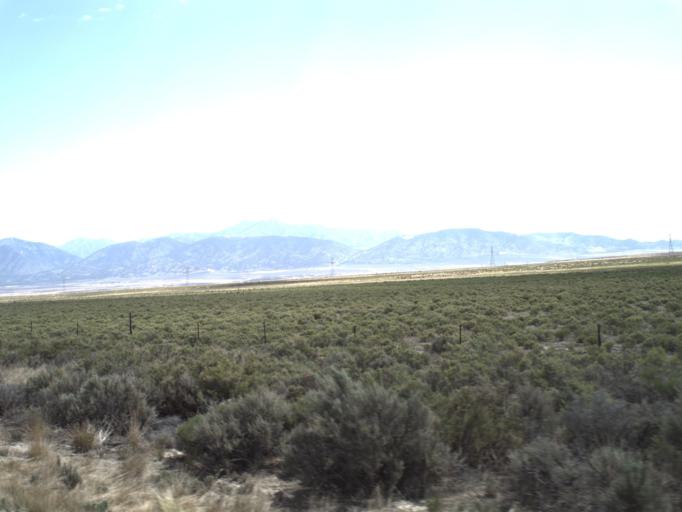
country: US
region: Utah
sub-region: Tooele County
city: Tooele
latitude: 40.2203
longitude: -112.4053
